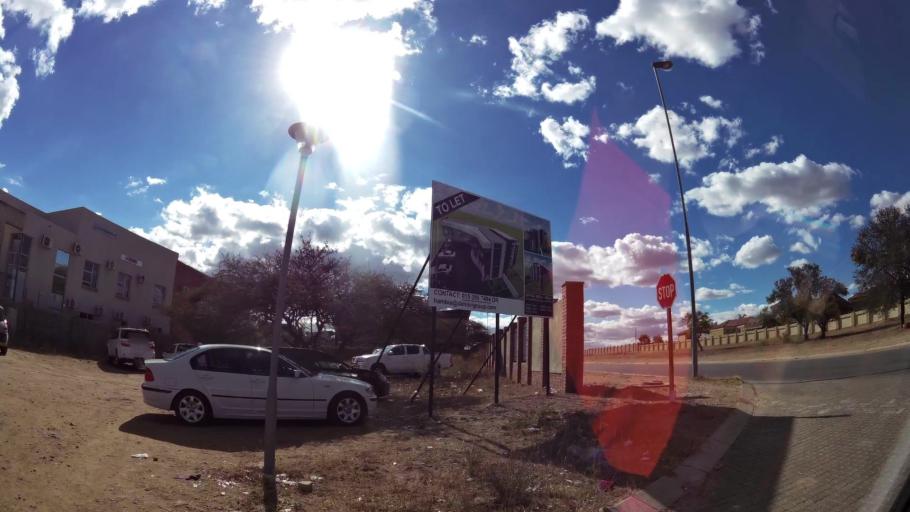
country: ZA
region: Limpopo
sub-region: Capricorn District Municipality
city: Polokwane
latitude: -23.8892
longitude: 29.4752
